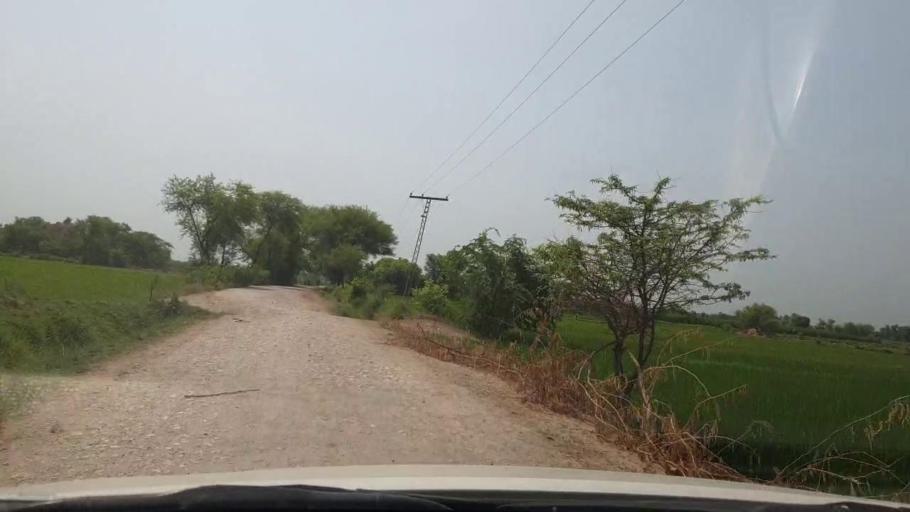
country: PK
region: Sindh
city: Shikarpur
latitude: 27.9890
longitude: 68.7130
